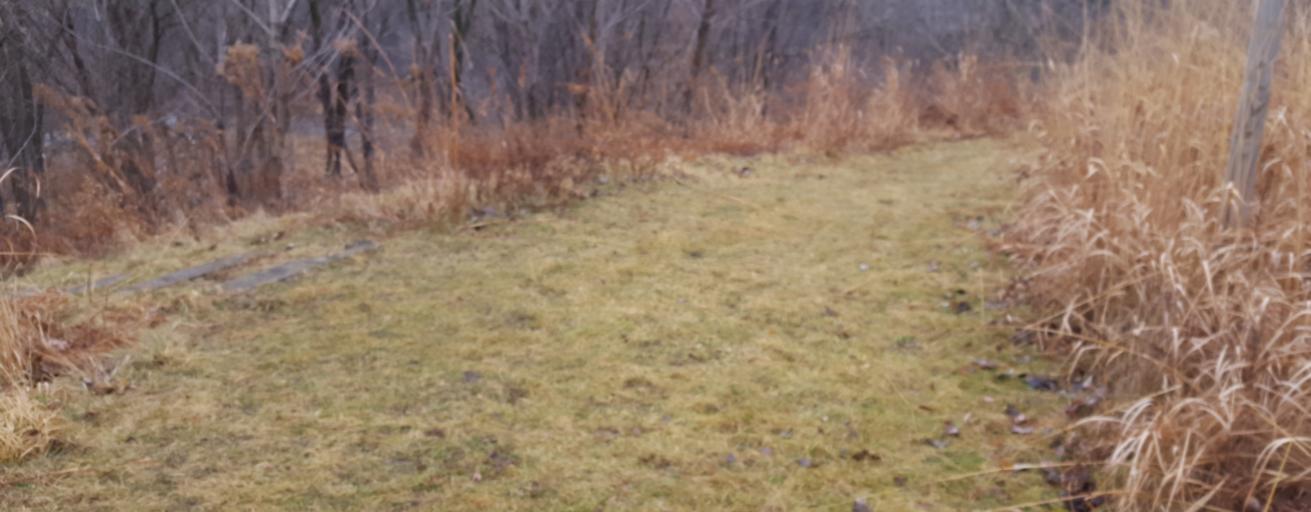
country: US
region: Illinois
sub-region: Cook County
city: Northfield
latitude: 42.0943
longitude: -87.8077
